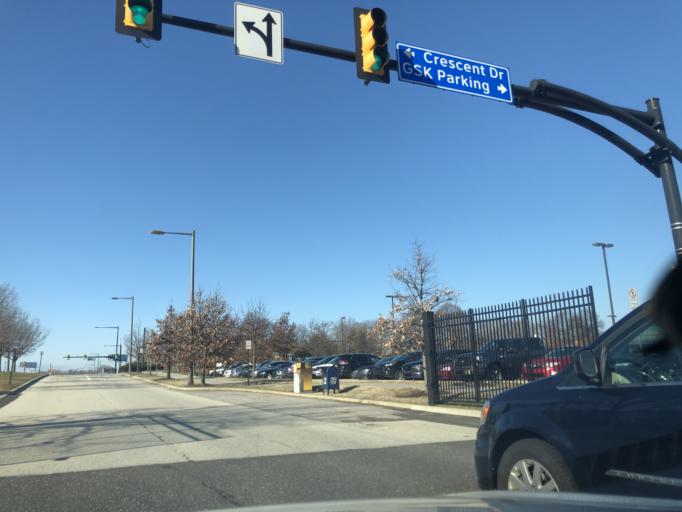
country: US
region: New Jersey
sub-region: Gloucester County
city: National Park
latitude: 39.8972
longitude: -75.1737
